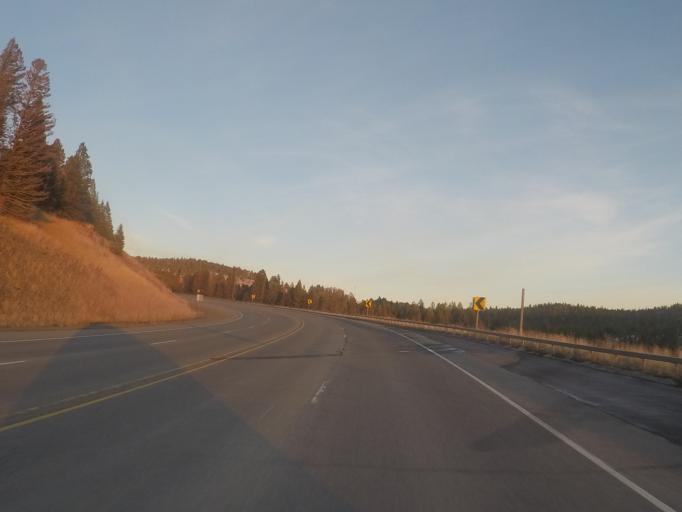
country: US
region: Montana
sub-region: Lewis and Clark County
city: Helena West Side
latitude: 46.5588
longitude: -112.3432
